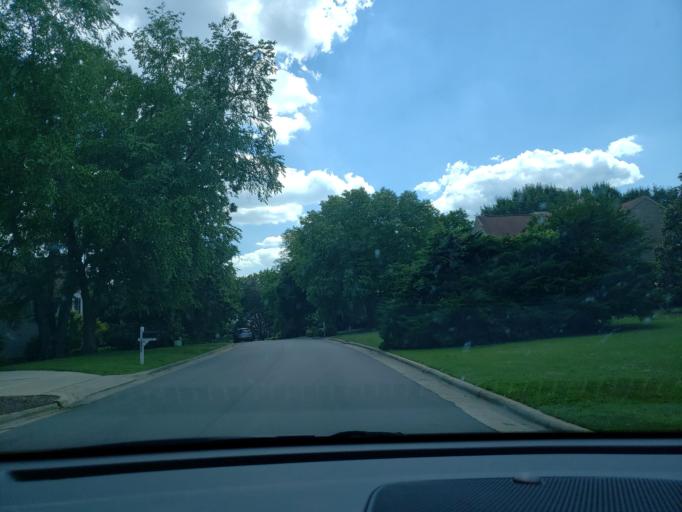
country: US
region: North Carolina
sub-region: Orange County
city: Chapel Hill
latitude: 35.9692
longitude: -78.9896
